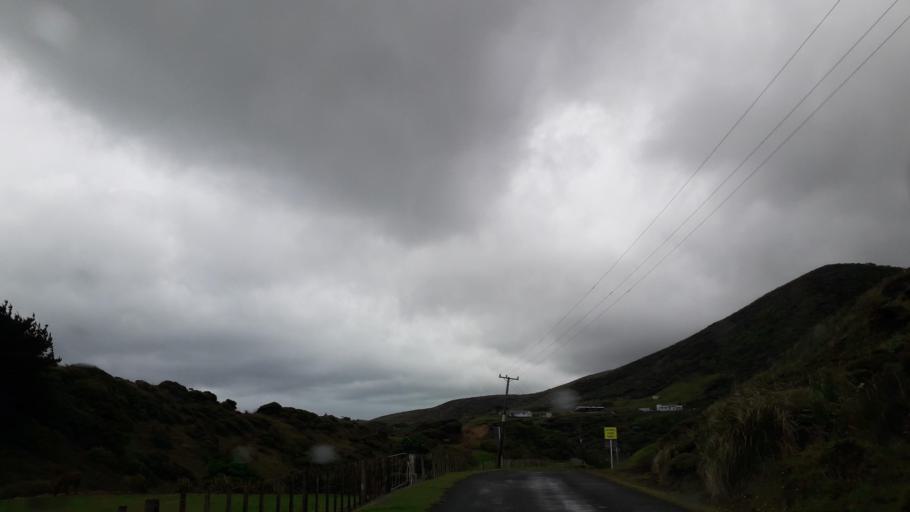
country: NZ
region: Northland
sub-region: Far North District
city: Ahipara
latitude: -35.4363
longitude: 173.2842
